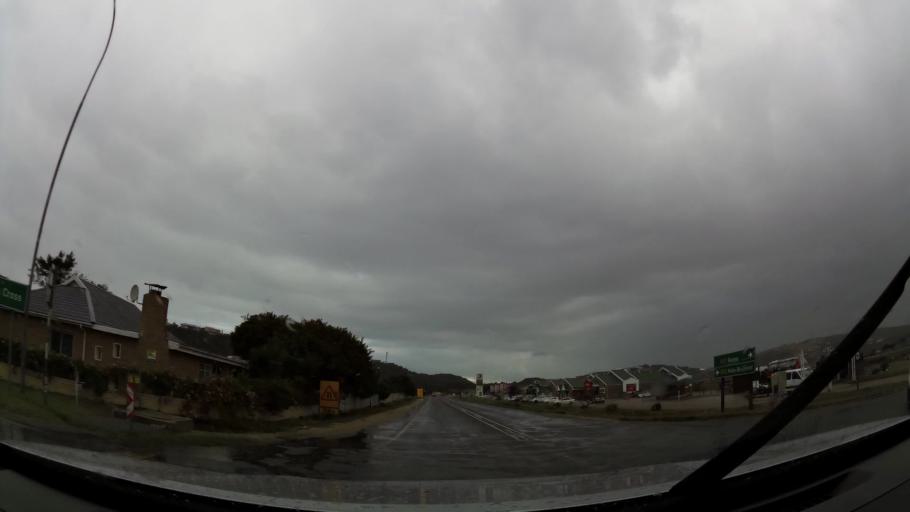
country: ZA
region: Western Cape
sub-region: Eden District Municipality
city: Mossel Bay
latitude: -34.0534
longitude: 22.2273
